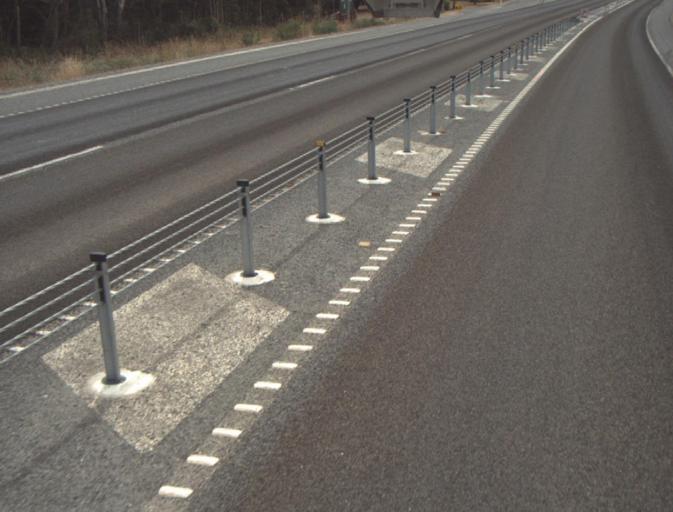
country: AU
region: Tasmania
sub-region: Launceston
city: Mayfield
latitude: -41.2957
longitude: 147.0491
